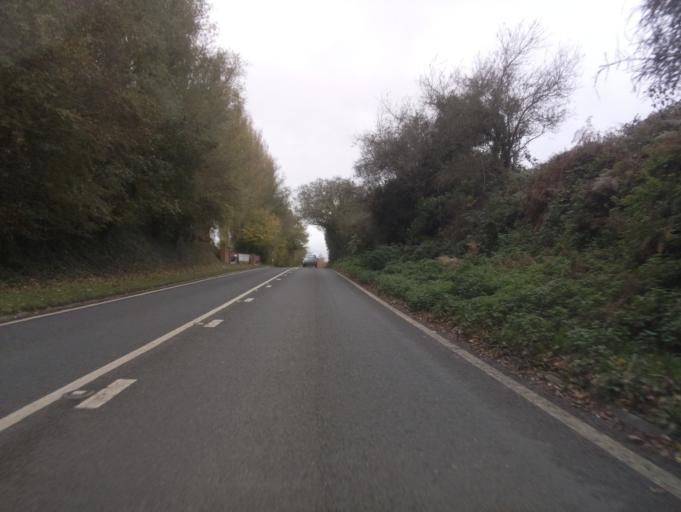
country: GB
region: England
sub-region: Somerset
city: South Petherton
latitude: 50.9349
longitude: -2.8165
